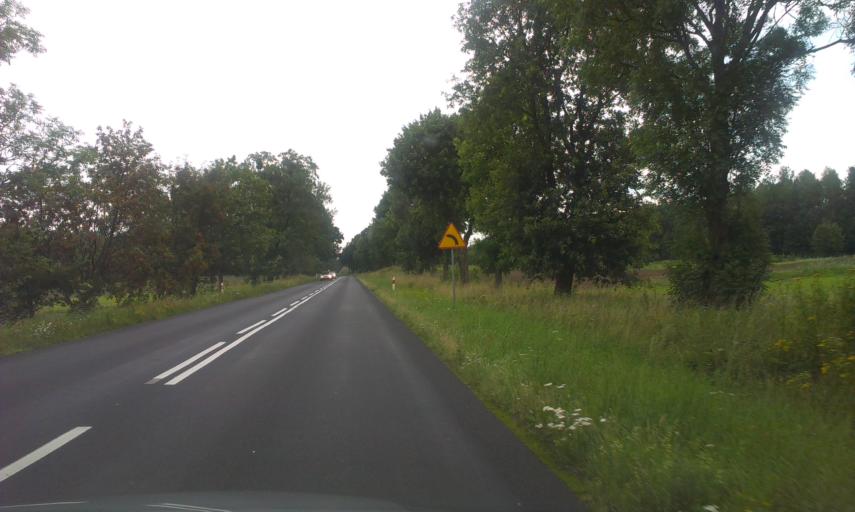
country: PL
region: West Pomeranian Voivodeship
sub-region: Powiat swidwinski
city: Polczyn-Zdroj
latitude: 53.8496
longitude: 16.0747
